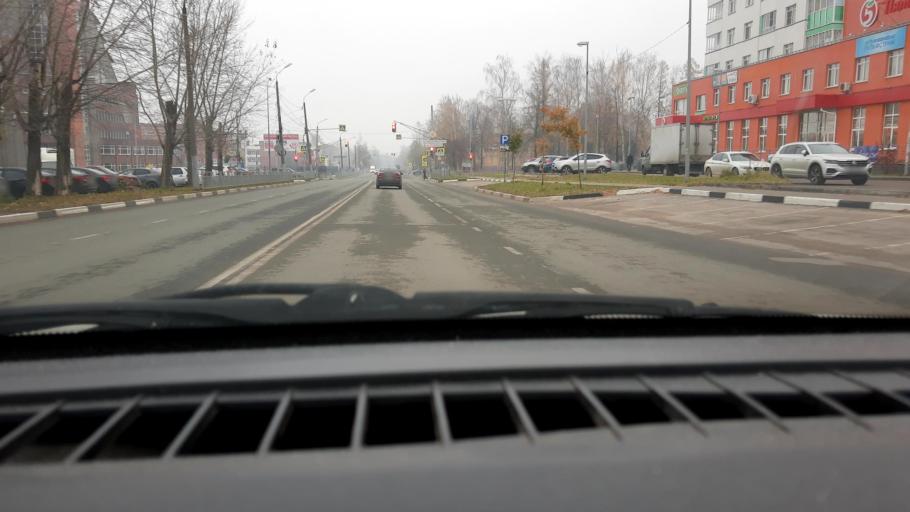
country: RU
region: Nizjnij Novgorod
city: Kstovo
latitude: 56.1507
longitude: 44.1865
